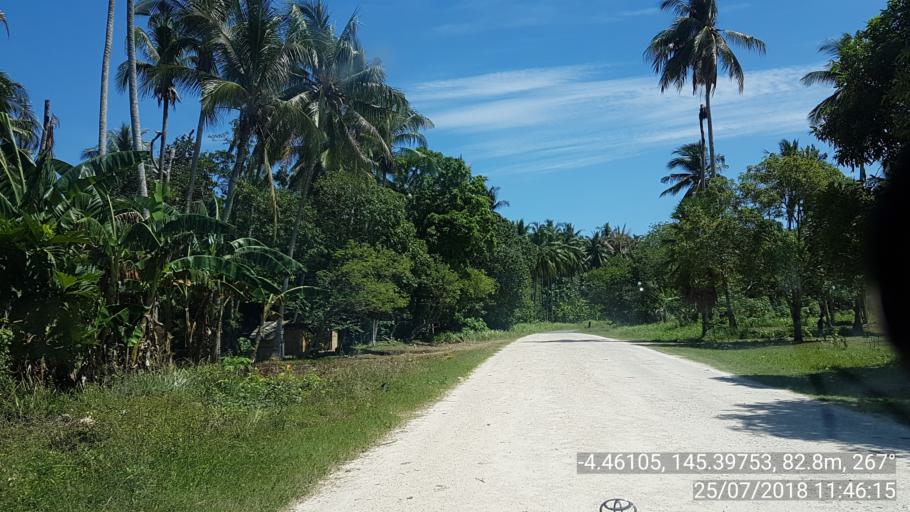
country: PG
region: Madang
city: Madang
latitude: -4.4611
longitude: 145.3975
